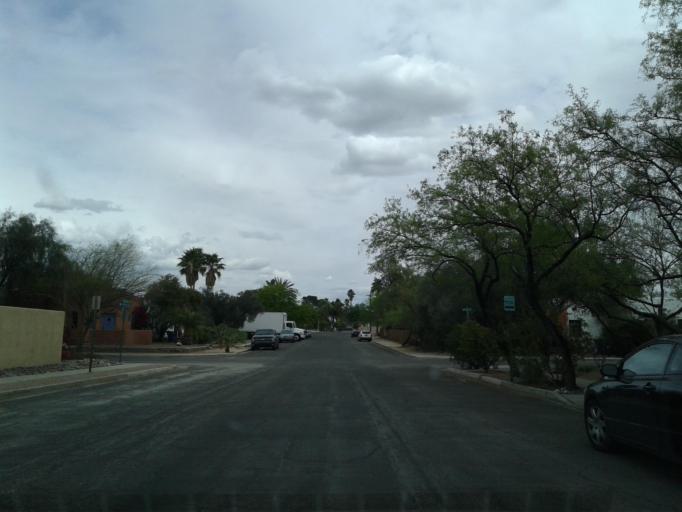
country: US
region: Arizona
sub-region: Pima County
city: Tucson
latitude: 32.2339
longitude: -110.9371
